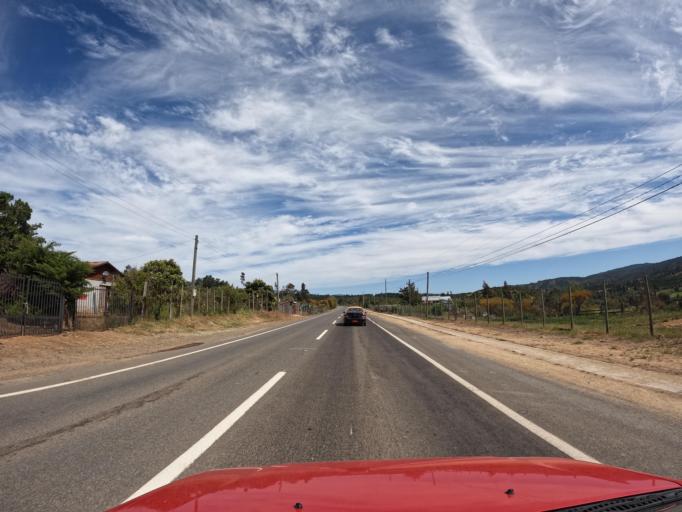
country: CL
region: Maule
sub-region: Provincia de Talca
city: Talca
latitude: -35.1231
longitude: -71.9578
